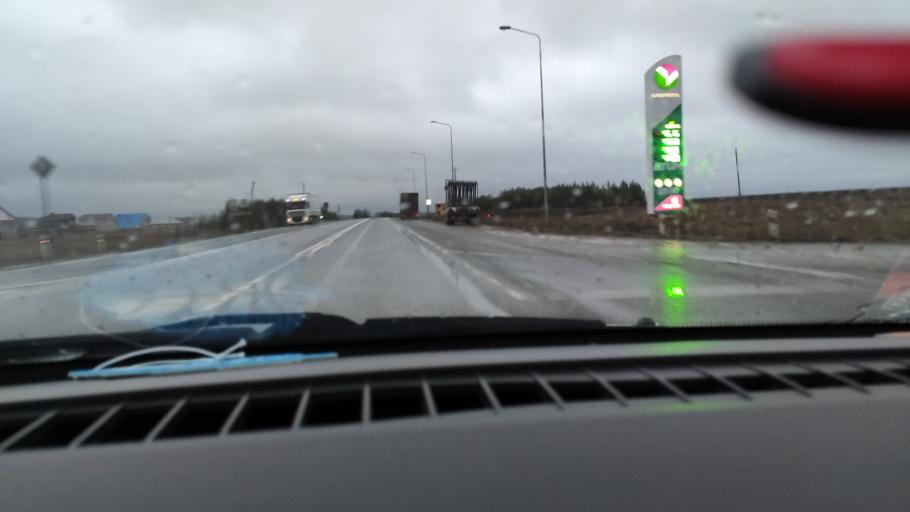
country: RU
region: Udmurtiya
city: Alnashi
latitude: 56.1712
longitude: 52.4748
